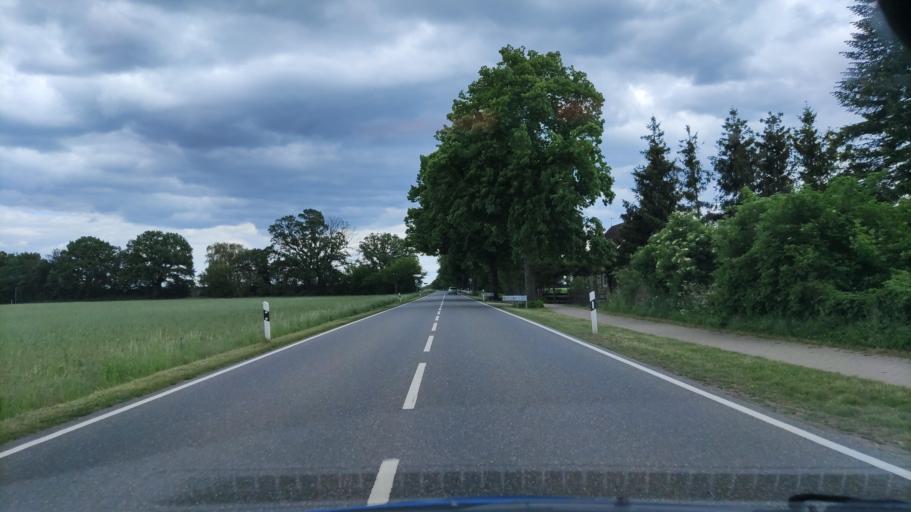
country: DE
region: Mecklenburg-Vorpommern
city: Lubz
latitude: 53.4644
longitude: 12.1325
